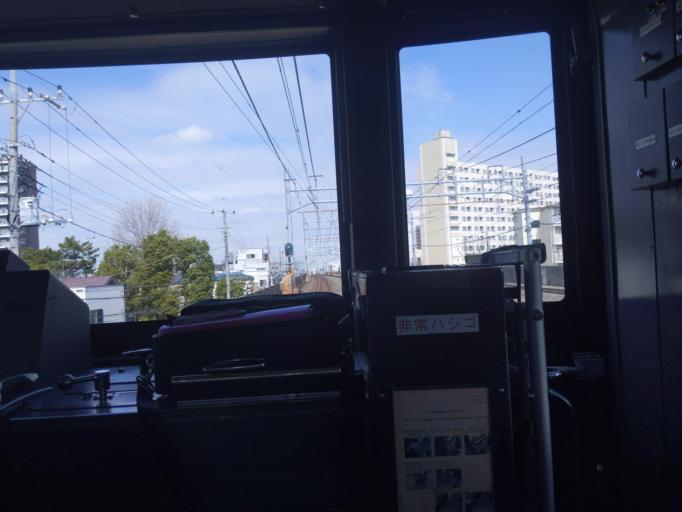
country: JP
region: Saitama
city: Soka
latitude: 35.8003
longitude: 139.7929
